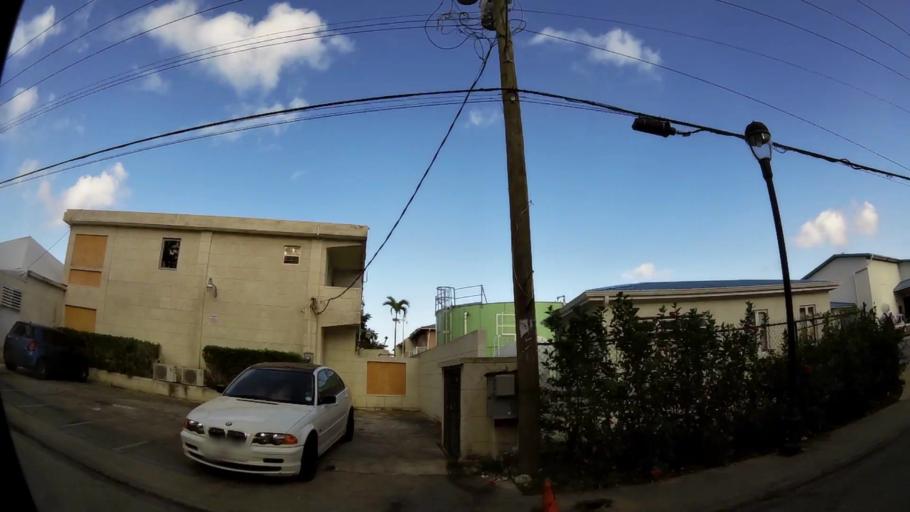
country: BB
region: Christ Church
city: Oistins
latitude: 13.0658
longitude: -59.5645
